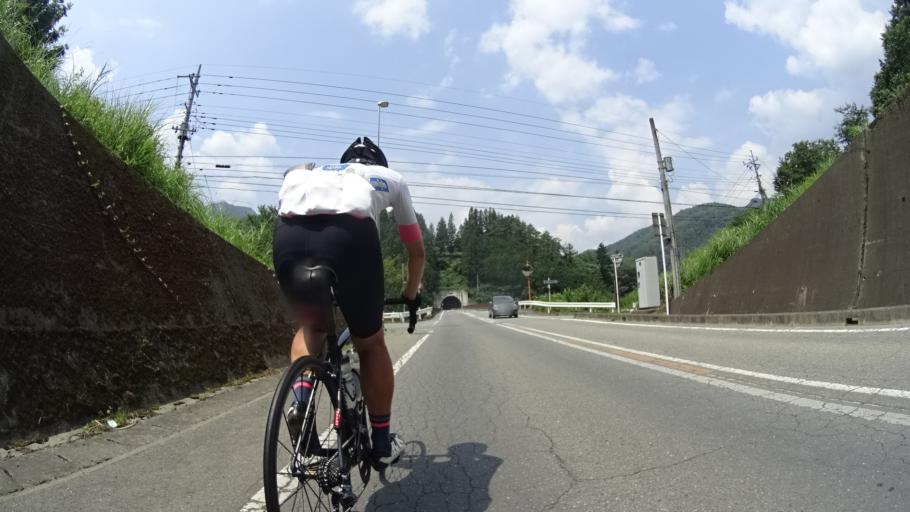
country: JP
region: Gunma
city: Tomioka
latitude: 36.0830
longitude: 138.7644
